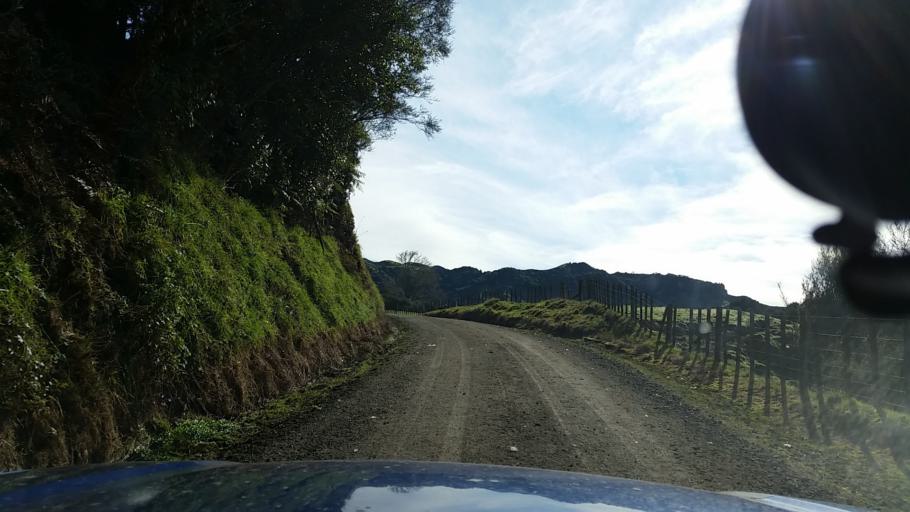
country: NZ
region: Taranaki
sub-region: New Plymouth District
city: Waitara
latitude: -39.0572
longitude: 174.7743
